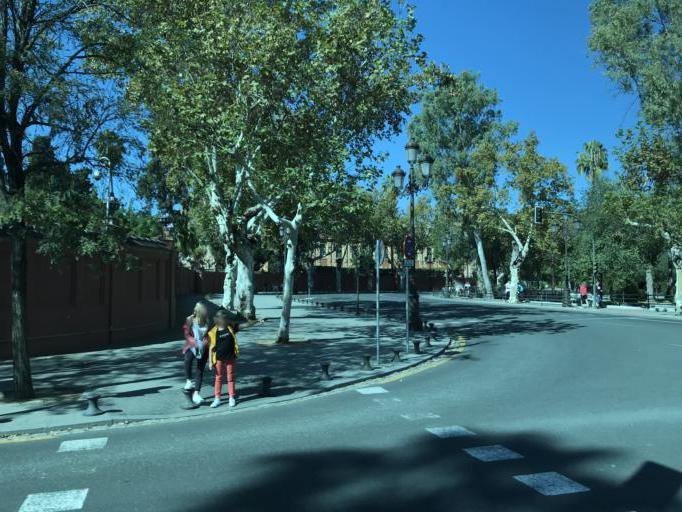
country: ES
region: Andalusia
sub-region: Provincia de Sevilla
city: Sevilla
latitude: 37.3797
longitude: -5.9920
